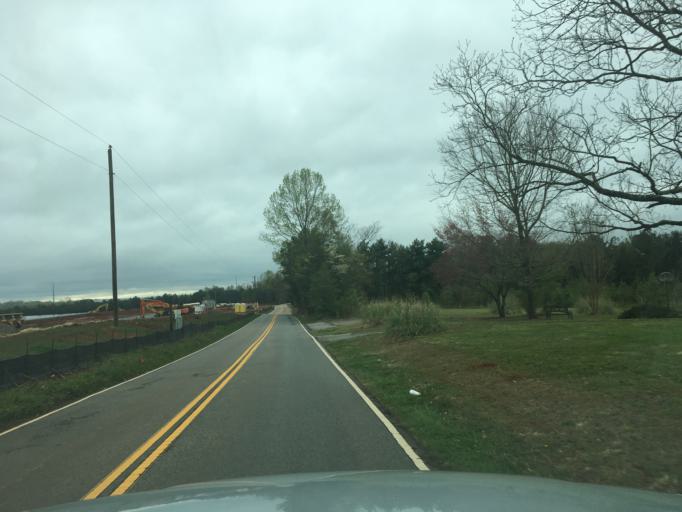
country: US
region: South Carolina
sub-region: Spartanburg County
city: Fairforest
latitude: 34.9674
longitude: -82.0502
